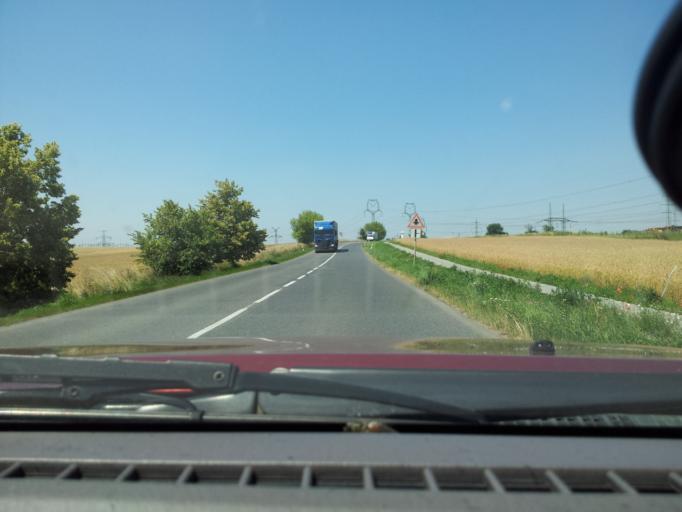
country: CZ
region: South Moravian
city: Telnice
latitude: 49.1052
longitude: 16.7150
